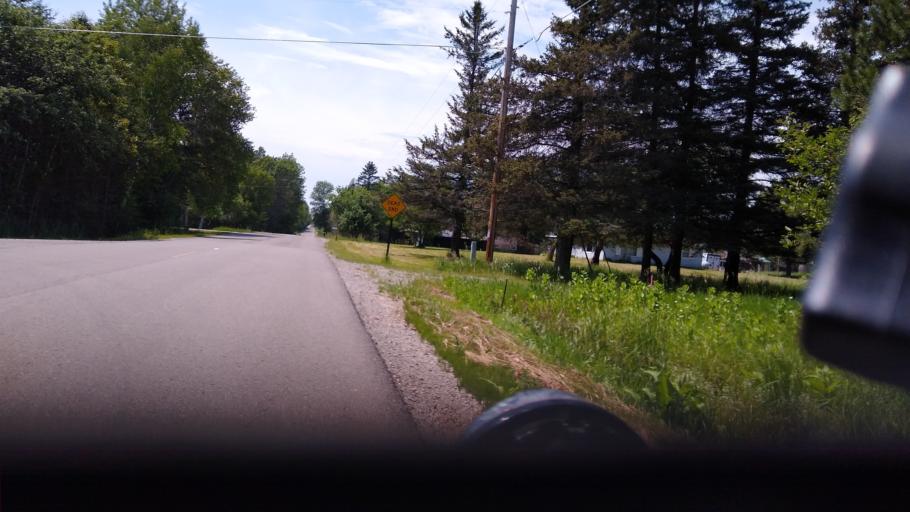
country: US
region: Michigan
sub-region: Delta County
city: Escanaba
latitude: 45.7101
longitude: -87.1317
